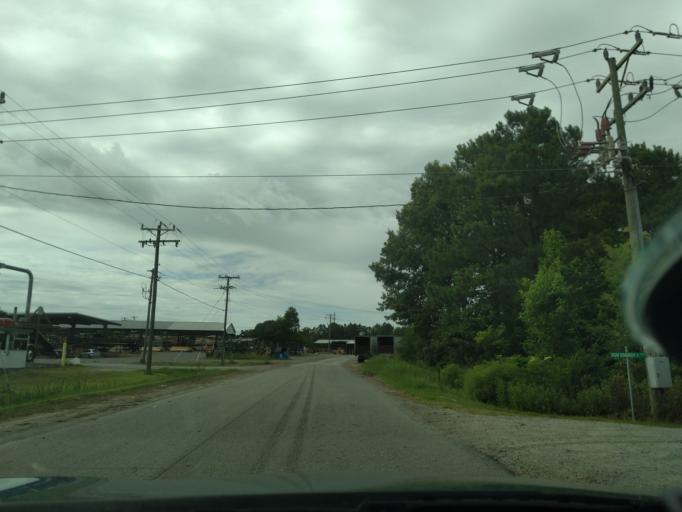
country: US
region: North Carolina
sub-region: Washington County
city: Plymouth
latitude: 35.8726
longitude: -76.7128
